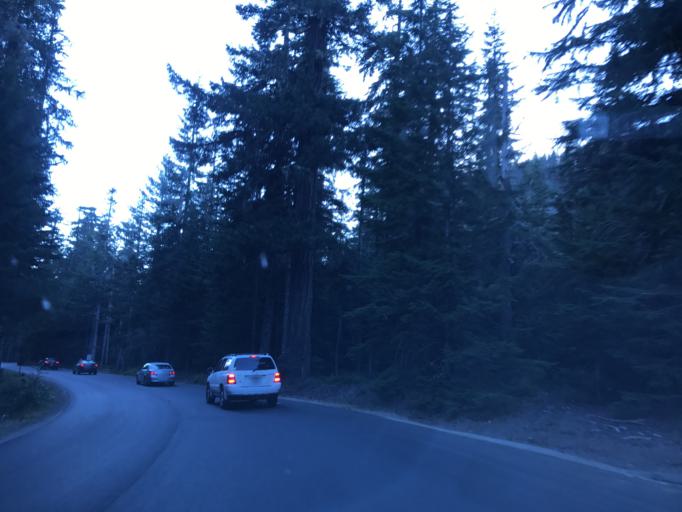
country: US
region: Washington
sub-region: Pierce County
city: Buckley
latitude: 46.7665
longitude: -121.7920
